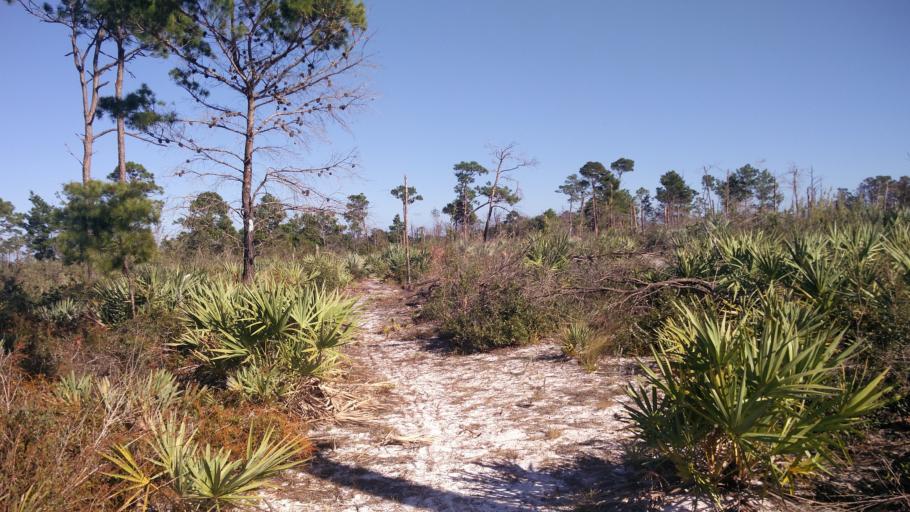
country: US
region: Florida
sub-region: Palm Beach County
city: Tequesta
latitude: 27.0061
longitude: -80.1212
